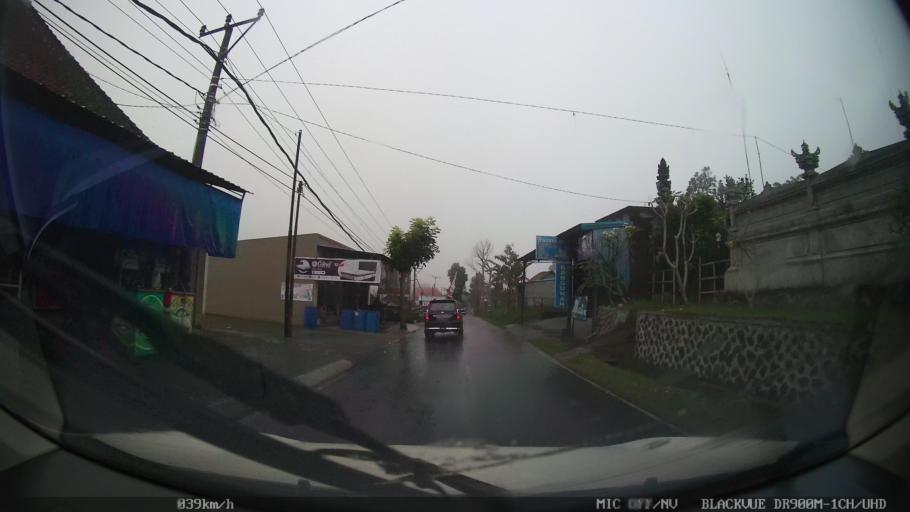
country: ID
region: Bali
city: Banjar Taro Kelod
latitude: -8.3169
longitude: 115.2995
